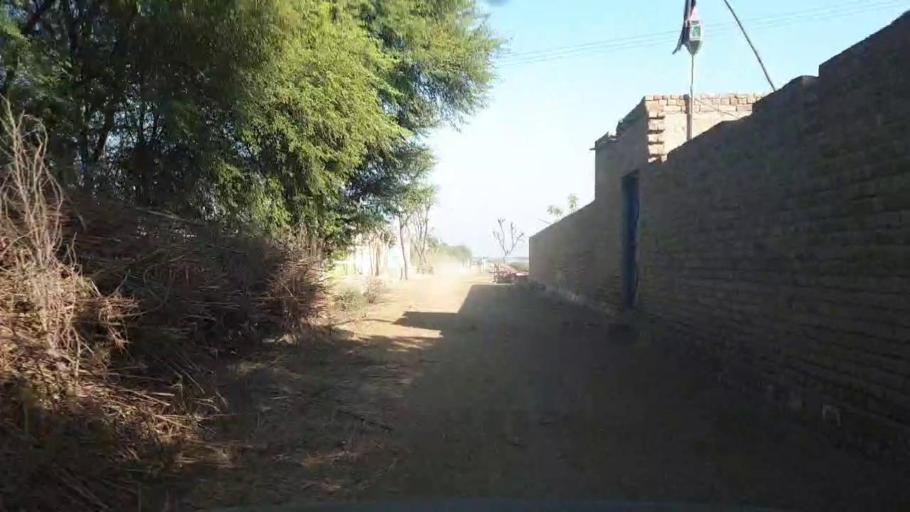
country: PK
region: Sindh
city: Sakrand
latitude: 26.0354
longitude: 68.4455
